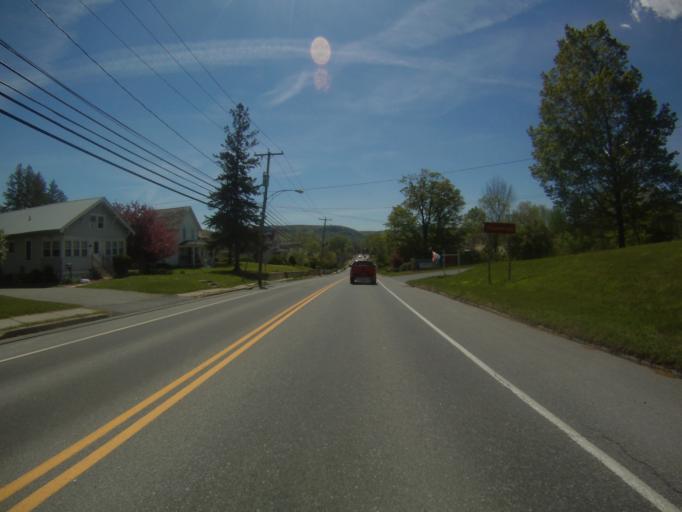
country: US
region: New York
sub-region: Essex County
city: Ticonderoga
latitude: 43.8516
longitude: -73.4367
